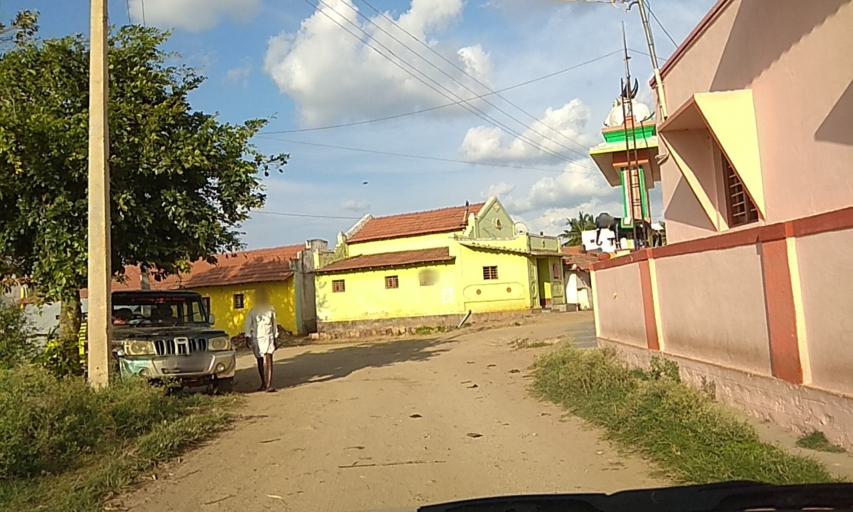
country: IN
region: Karnataka
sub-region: Chamrajnagar
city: Gundlupet
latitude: 11.7709
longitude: 76.7841
